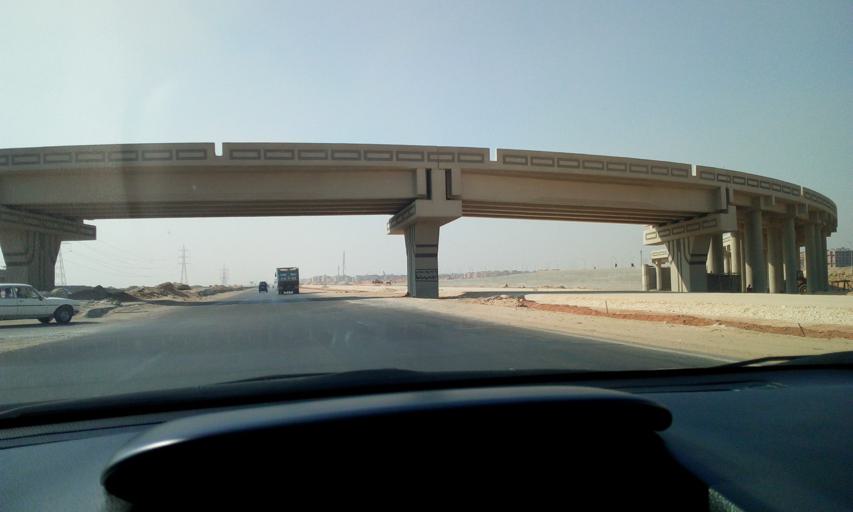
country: EG
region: Al Jizah
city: Madinat Sittah Uktubar
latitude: 29.9111
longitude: 31.0899
